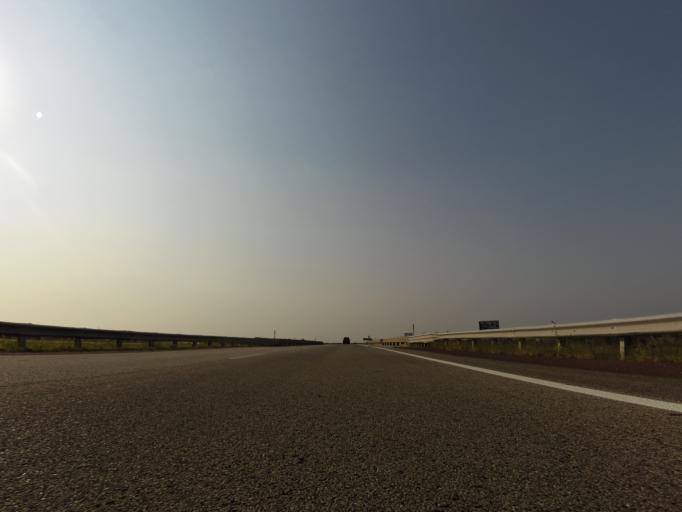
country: US
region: Kansas
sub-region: Reno County
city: South Hutchinson
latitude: 37.9404
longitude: -97.8807
